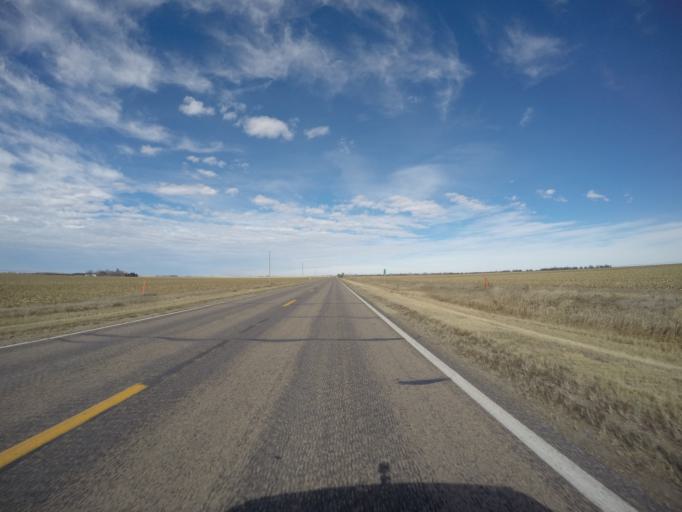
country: US
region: Nebraska
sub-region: Franklin County
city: Franklin
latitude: 40.2432
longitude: -98.9524
